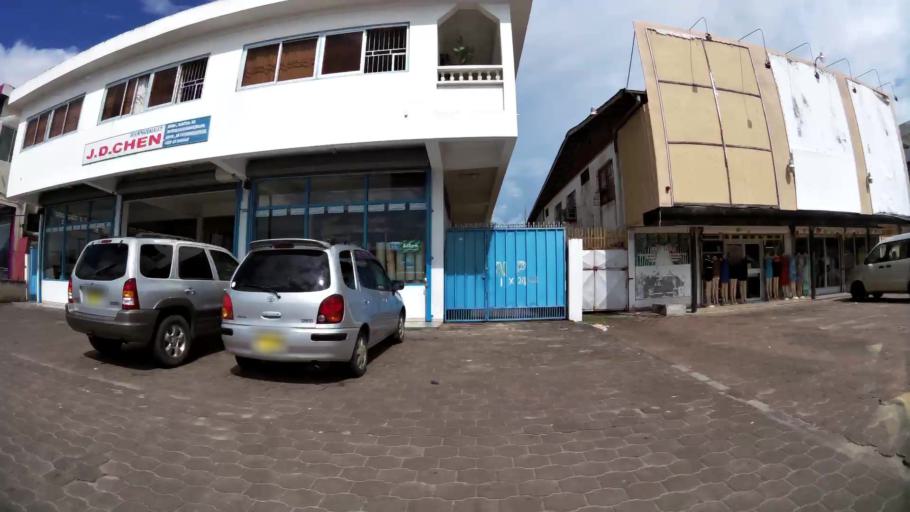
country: SR
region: Paramaribo
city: Paramaribo
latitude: 5.8400
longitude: -55.1451
